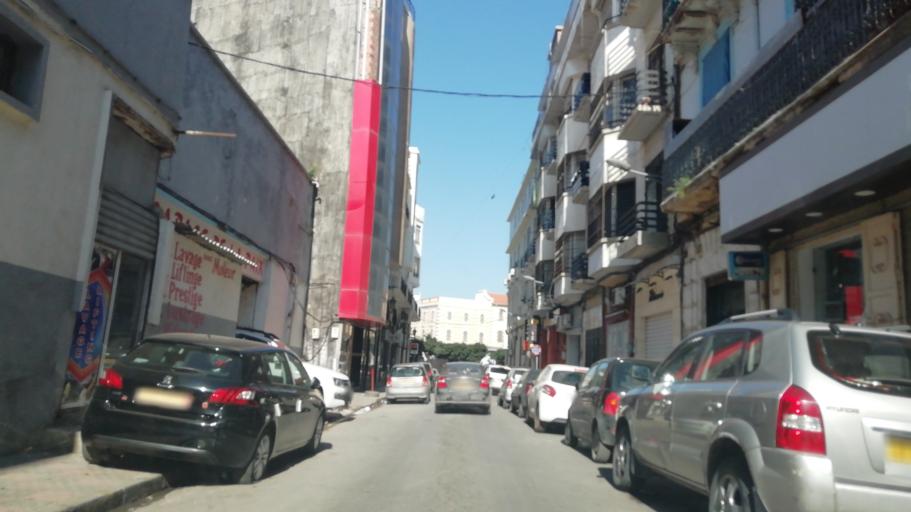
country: DZ
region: Oran
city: Oran
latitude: 35.7035
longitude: -0.6458
